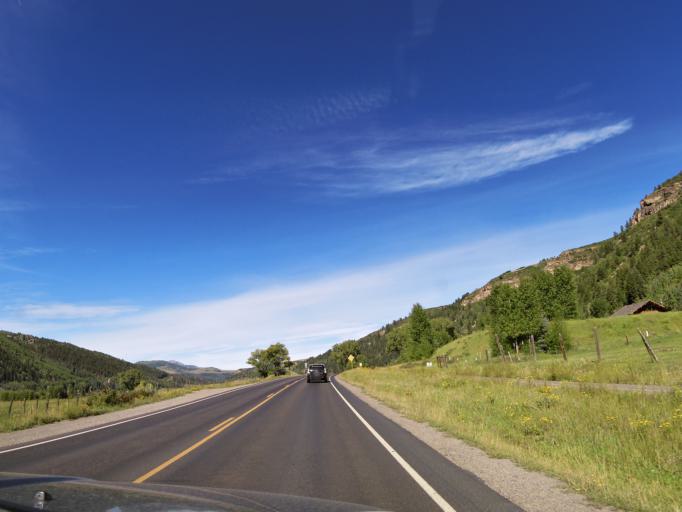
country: US
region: Colorado
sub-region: San Miguel County
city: Mountain Village
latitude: 37.9482
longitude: -107.8466
